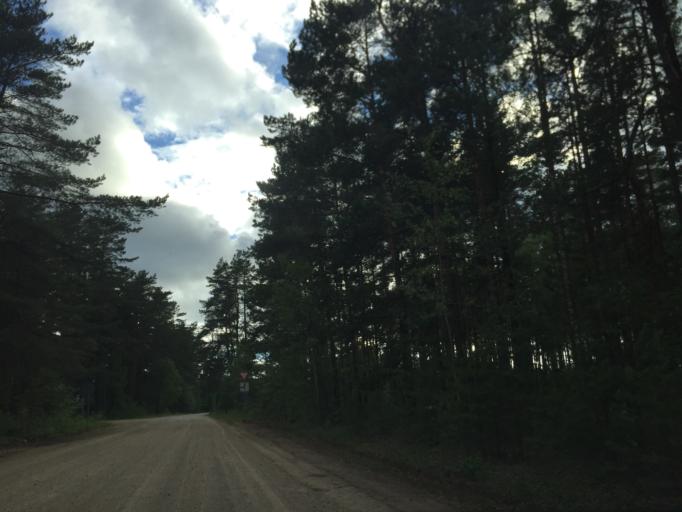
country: LV
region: Adazi
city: Adazi
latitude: 57.1259
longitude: 24.3356
